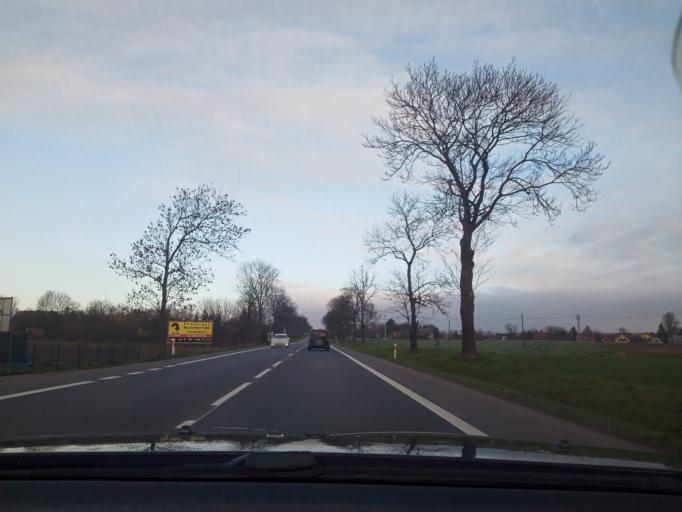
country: PL
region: Lesser Poland Voivodeship
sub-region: Powiat krakowski
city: Slomniki
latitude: 50.2610
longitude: 20.0798
